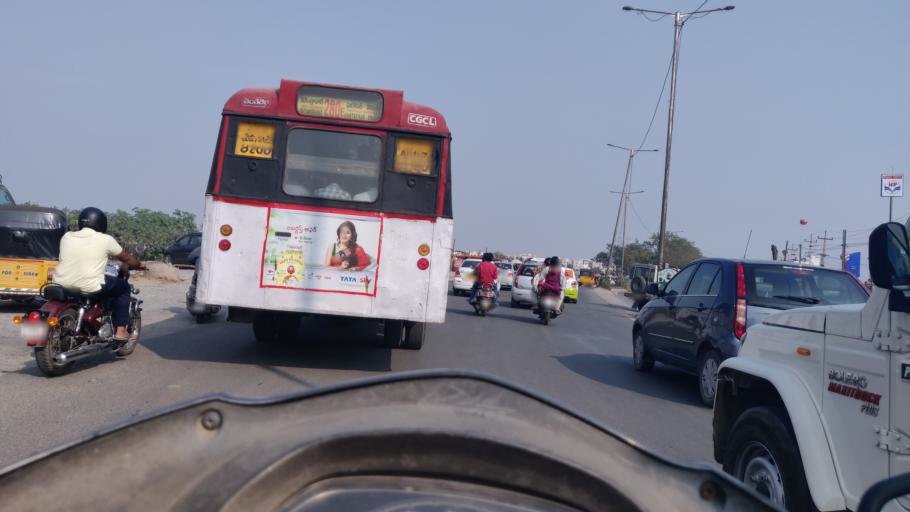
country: IN
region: Telangana
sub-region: Rangareddi
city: Uppal Kalan
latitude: 17.4022
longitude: 78.5756
